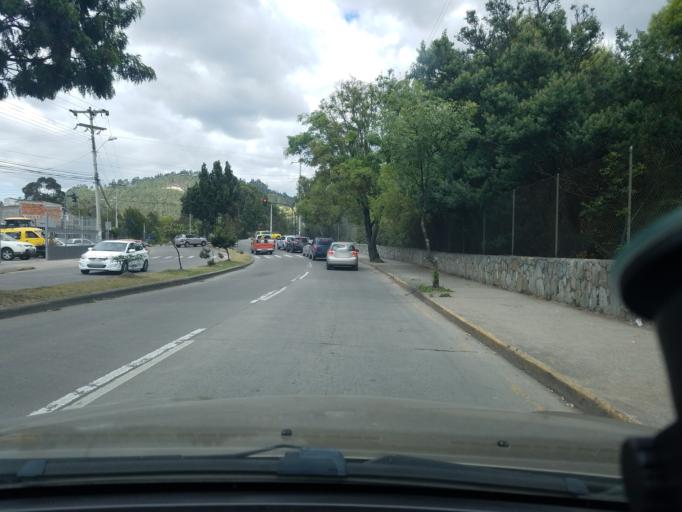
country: EC
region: Azuay
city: Cuenca
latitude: -2.9147
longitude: -78.9946
